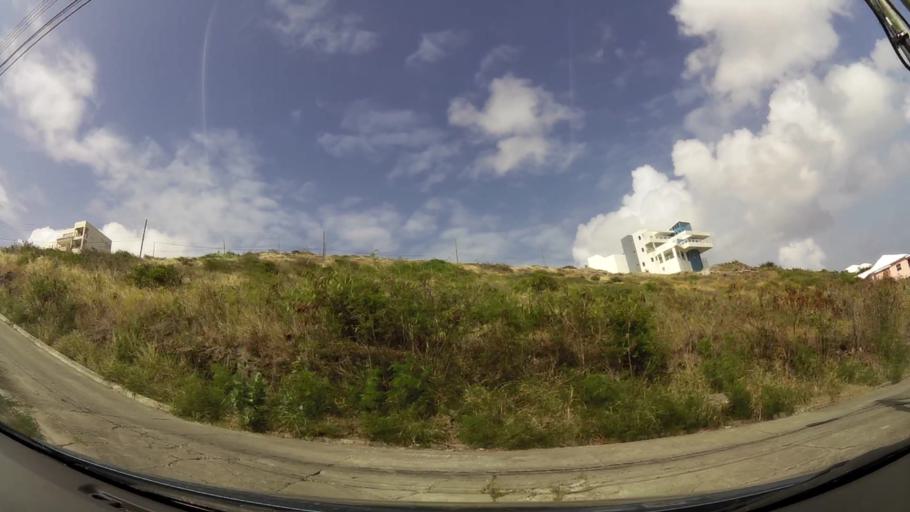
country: KN
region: Saint Peter Basseterre
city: Monkey Hill
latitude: 17.3019
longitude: -62.6943
